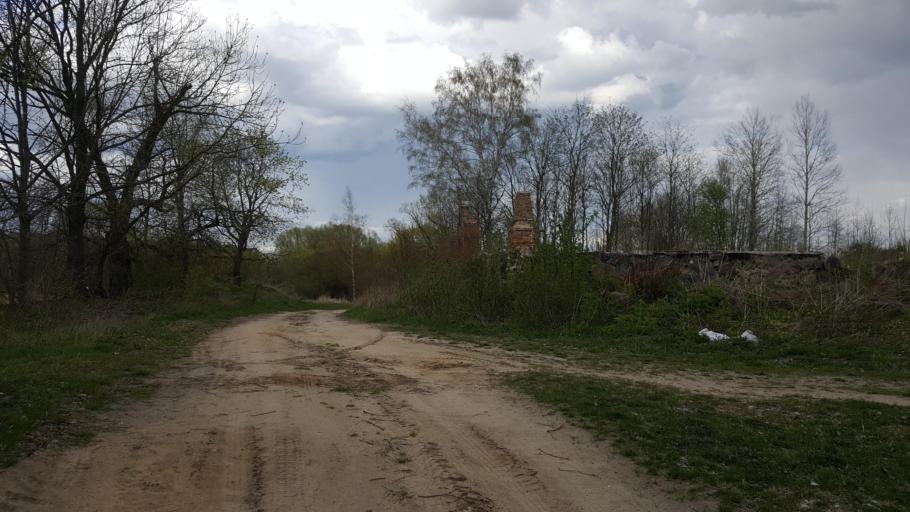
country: BY
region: Brest
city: Kamyanyets
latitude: 52.4061
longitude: 23.7092
